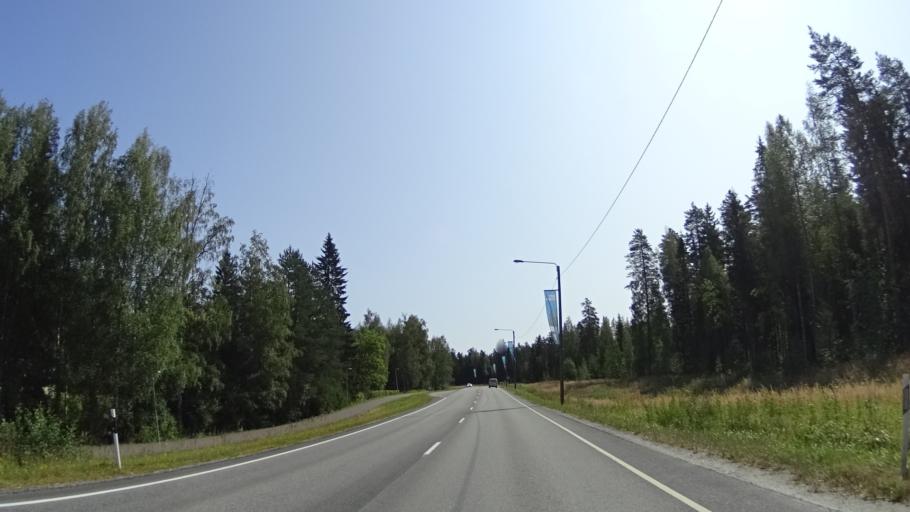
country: FI
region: Pirkanmaa
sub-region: Ylae-Pirkanmaa
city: Maenttae
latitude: 62.0293
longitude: 24.5871
